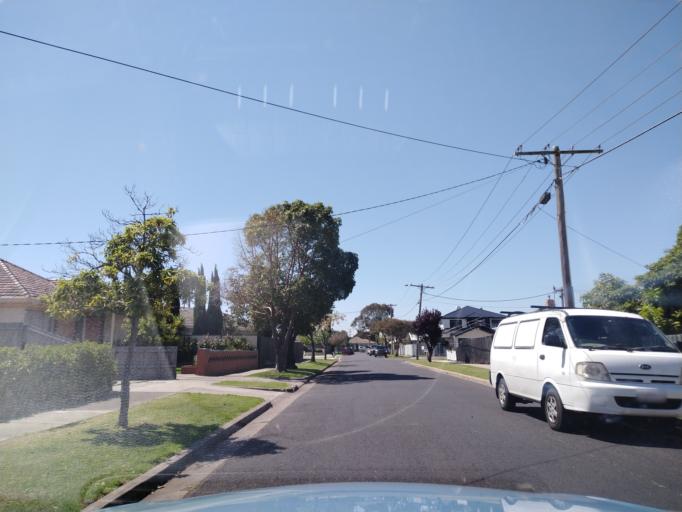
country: AU
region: Victoria
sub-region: Hobsons Bay
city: South Kingsville
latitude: -37.8339
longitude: 144.8596
